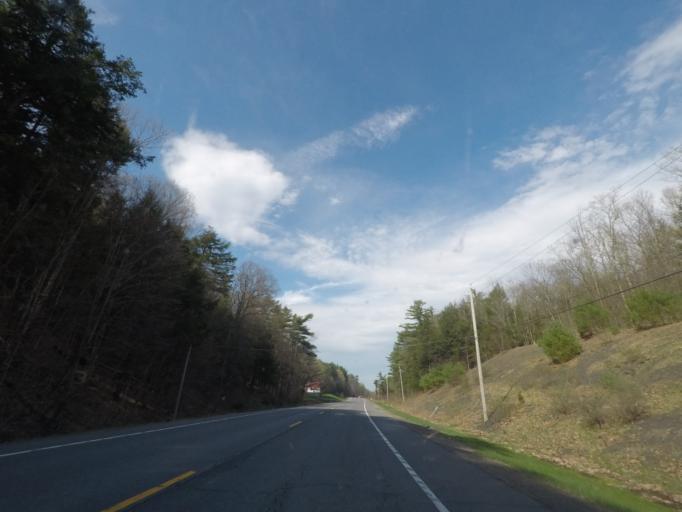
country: US
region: New York
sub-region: Albany County
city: Voorheesville
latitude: 42.5319
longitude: -73.9468
